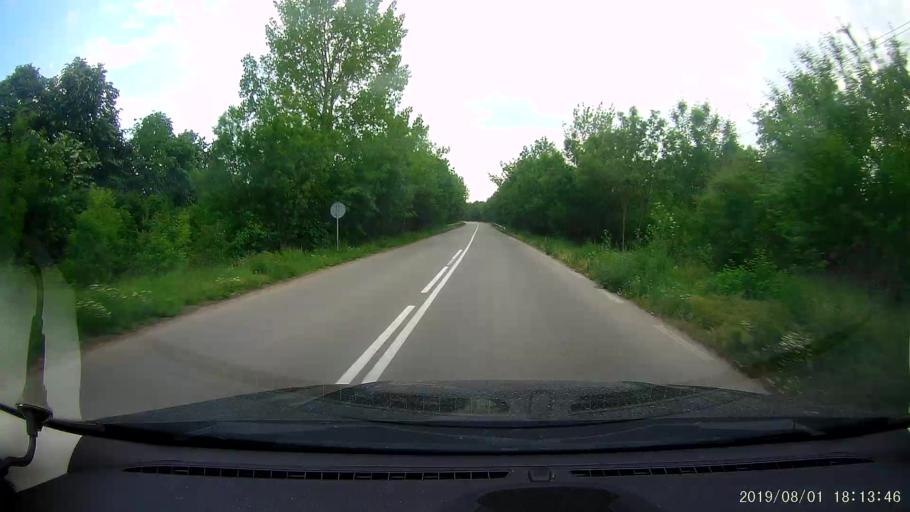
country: BG
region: Silistra
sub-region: Obshtina Dulovo
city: Dulovo
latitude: 43.7828
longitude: 27.1327
